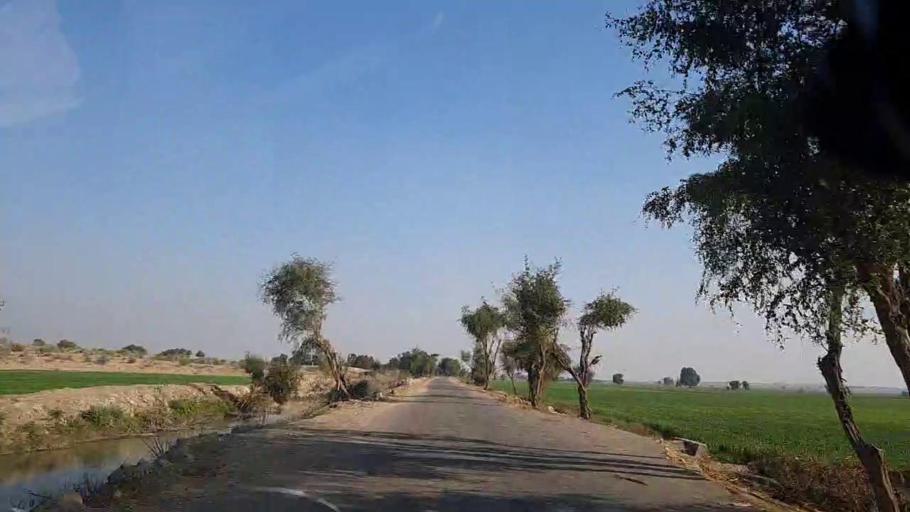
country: PK
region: Sindh
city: Khanpur
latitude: 27.6811
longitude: 69.5551
